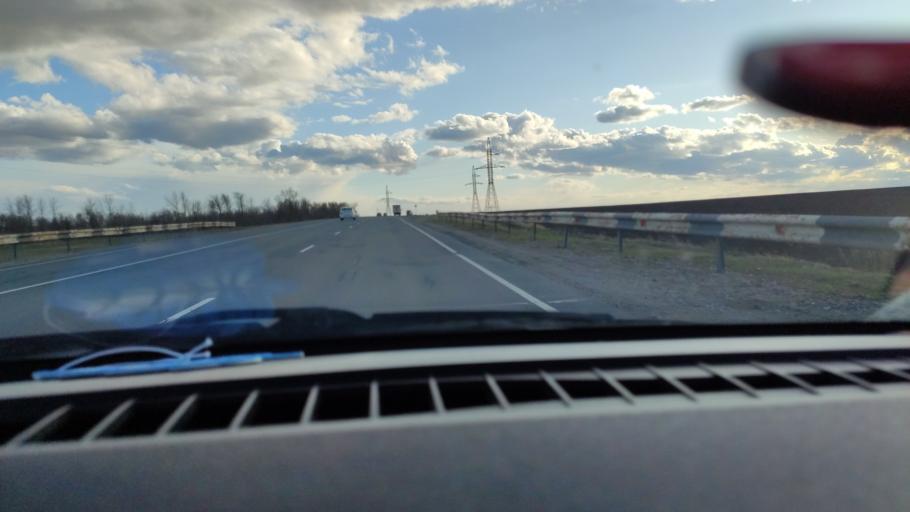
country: RU
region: Saratov
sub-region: Saratovskiy Rayon
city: Saratov
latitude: 51.7464
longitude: 46.0537
